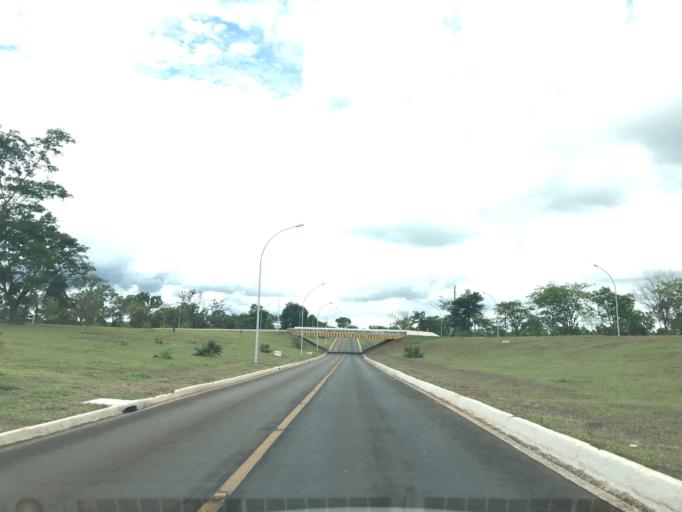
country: BR
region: Federal District
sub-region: Brasilia
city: Brasilia
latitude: -15.8026
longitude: -47.8505
